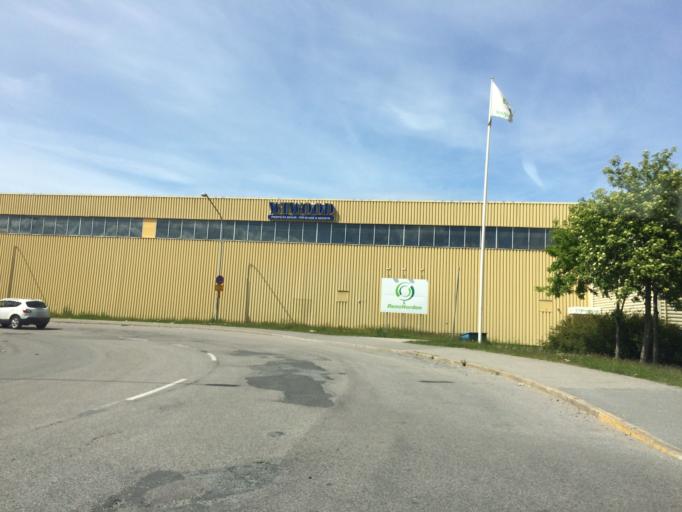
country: SE
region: Stockholm
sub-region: Huddinge Kommun
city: Huddinge
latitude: 59.2726
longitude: 18.0051
